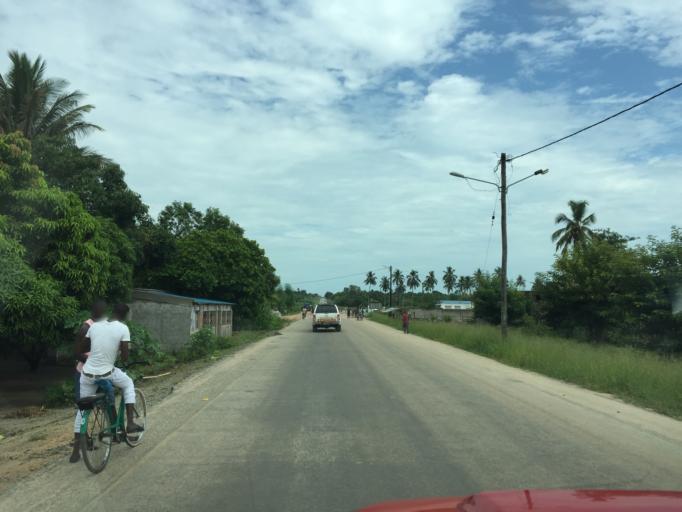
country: MZ
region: Zambezia
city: Quelimane
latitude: -17.5922
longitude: 36.8136
